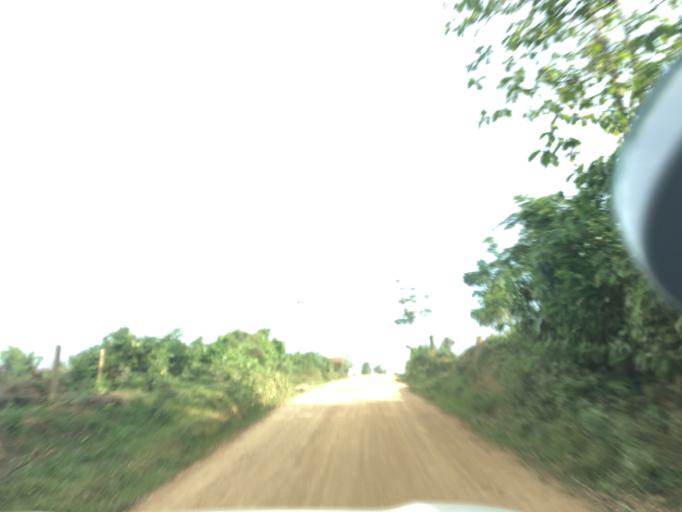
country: TH
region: Loei
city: Chiang Khan
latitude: 18.0115
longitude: 101.4202
